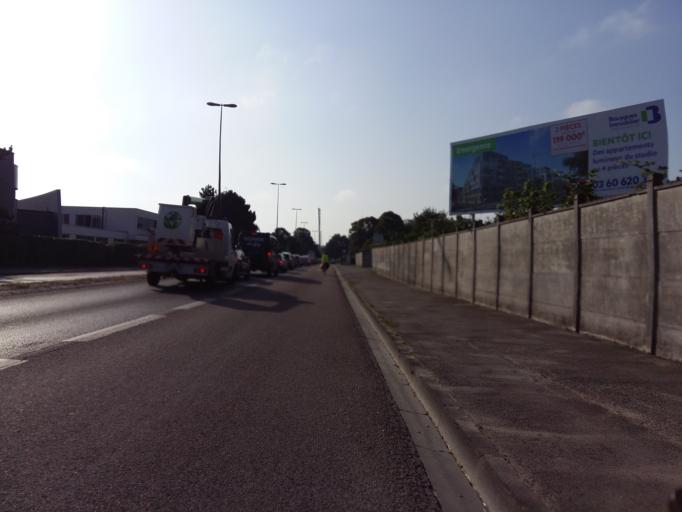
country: FR
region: Picardie
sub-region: Departement de la Somme
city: Amiens
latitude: 49.9012
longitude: 2.2852
